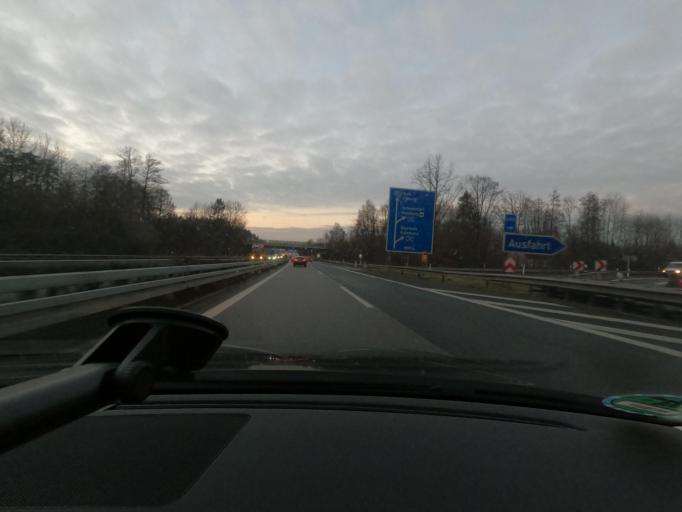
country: DE
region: Bavaria
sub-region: Upper Franconia
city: Gundelsheim
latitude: 49.9200
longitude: 10.9306
